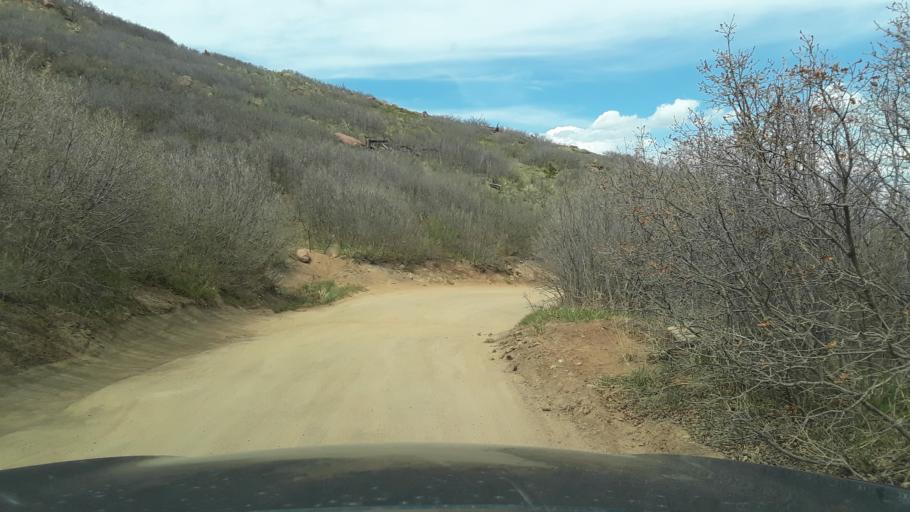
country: US
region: Colorado
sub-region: El Paso County
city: Palmer Lake
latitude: 39.0830
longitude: -104.9141
